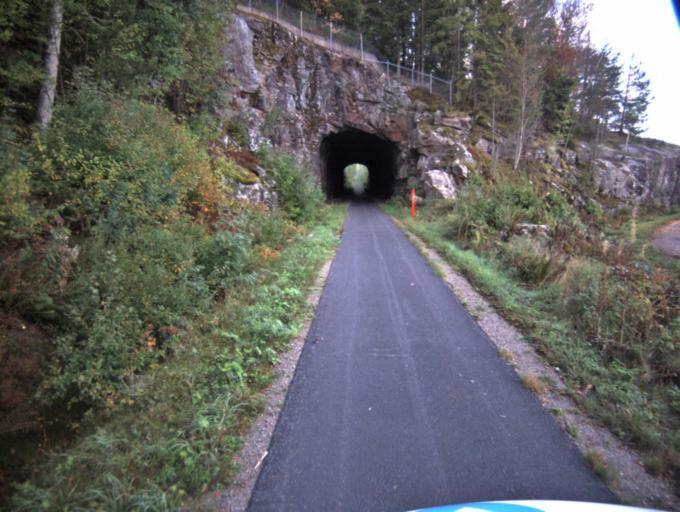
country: SE
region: Vaestra Goetaland
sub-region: Ulricehamns Kommun
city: Ulricehamn
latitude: 57.7551
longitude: 13.3975
